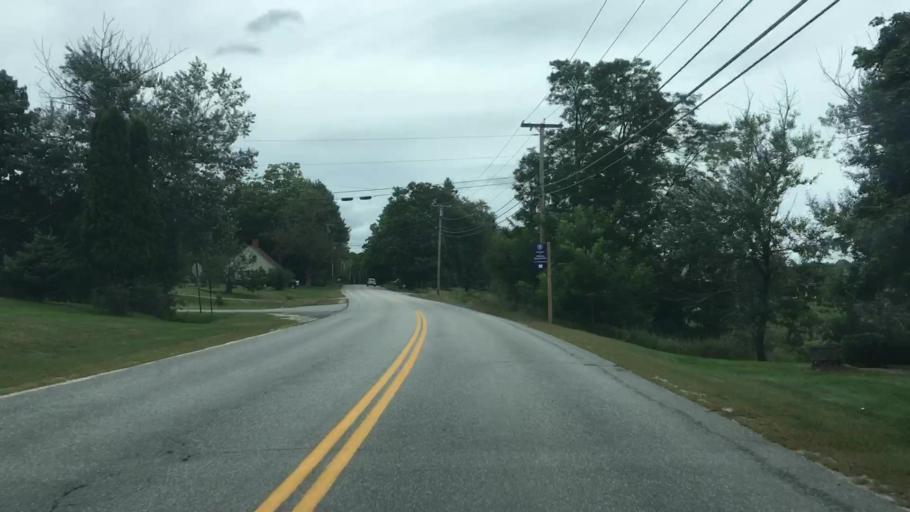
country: US
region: Maine
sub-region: Cumberland County
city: Yarmouth
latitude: 43.8289
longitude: -70.1964
